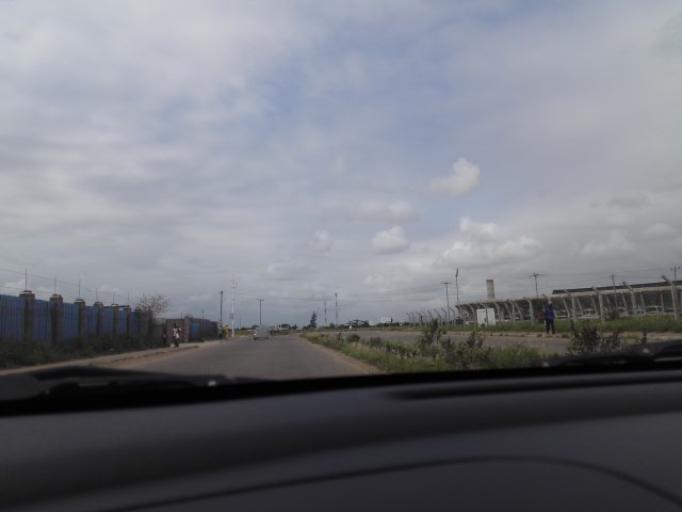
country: MZ
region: Maputo City
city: Maputo
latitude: -25.8253
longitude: 32.5802
